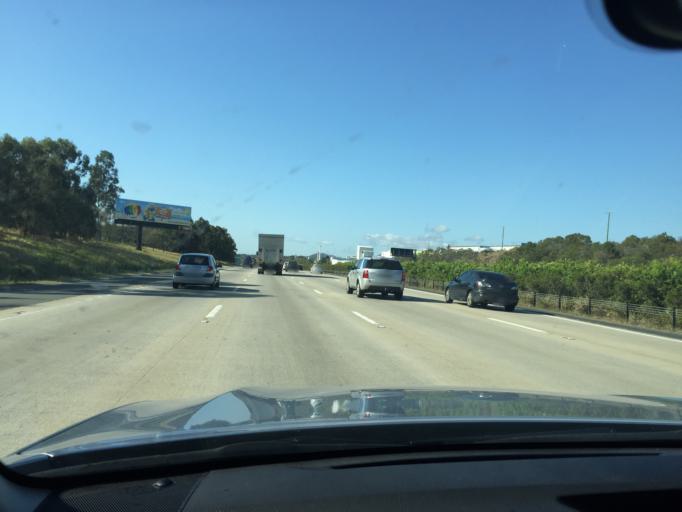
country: AU
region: Queensland
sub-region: Gold Coast
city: Yatala
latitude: -27.7469
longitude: 153.2342
